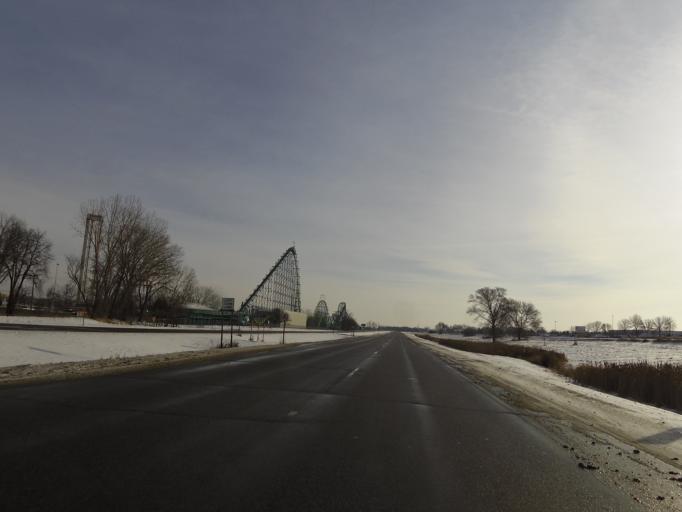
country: US
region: Minnesota
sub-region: Hennepin County
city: Eden Prairie
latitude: 44.7983
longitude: -93.4616
